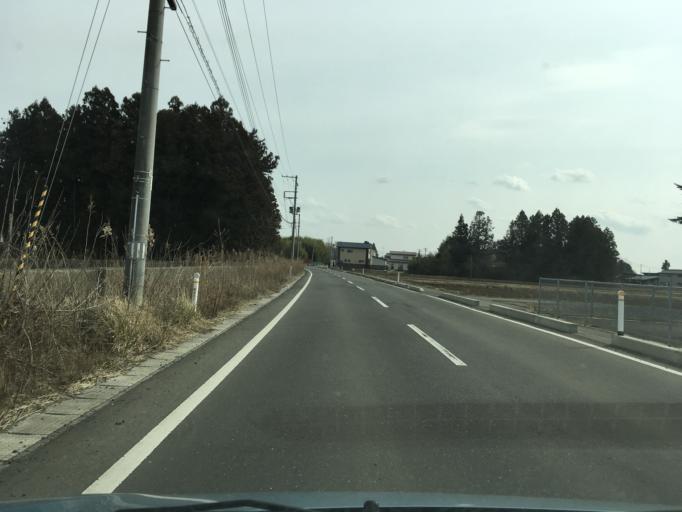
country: JP
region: Miyagi
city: Wakuya
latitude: 38.7214
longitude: 141.2412
